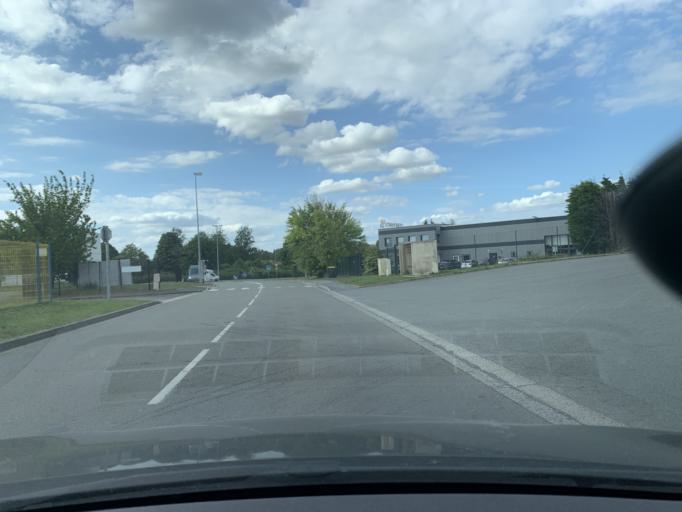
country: FR
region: Nord-Pas-de-Calais
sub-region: Departement du Nord
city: Proville
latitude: 50.1734
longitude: 3.1986
